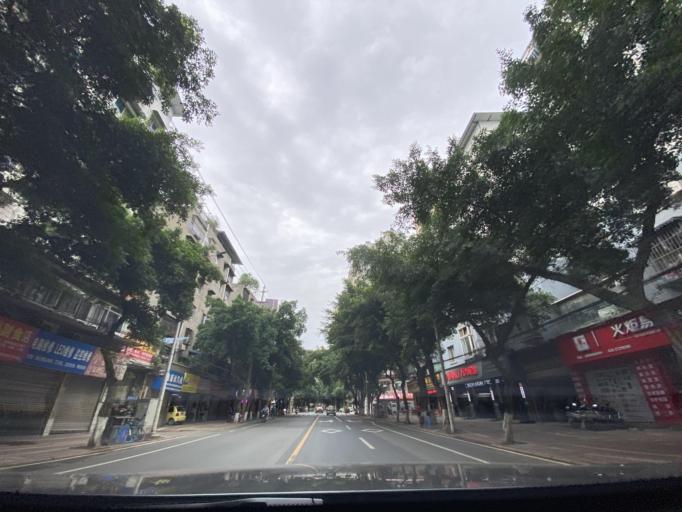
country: CN
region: Sichuan
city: Jiancheng
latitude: 30.3836
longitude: 104.5526
